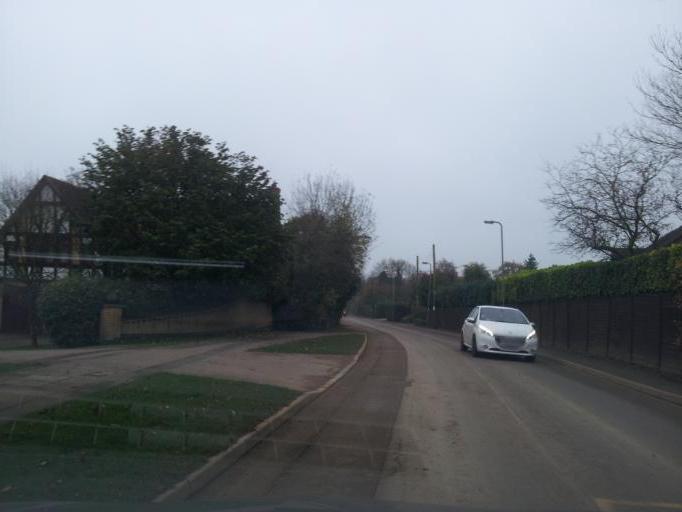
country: GB
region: England
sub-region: Northamptonshire
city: Brackley
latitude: 52.0393
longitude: -1.1434
